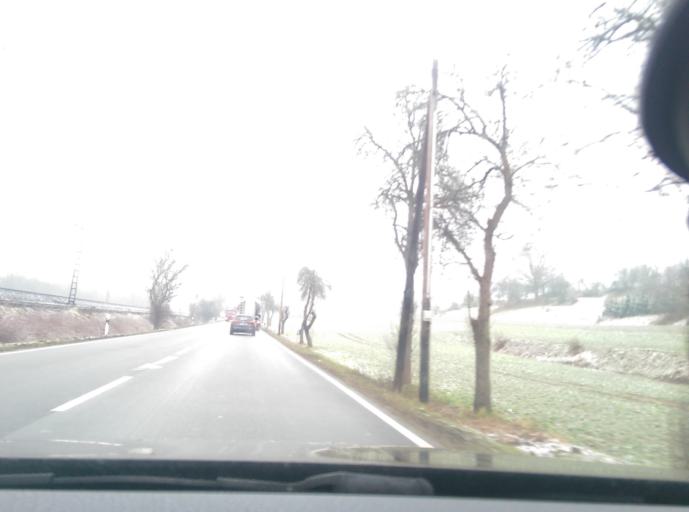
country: DE
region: Hesse
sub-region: Regierungsbezirk Kassel
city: Eschwege
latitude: 51.1758
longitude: 9.9888
